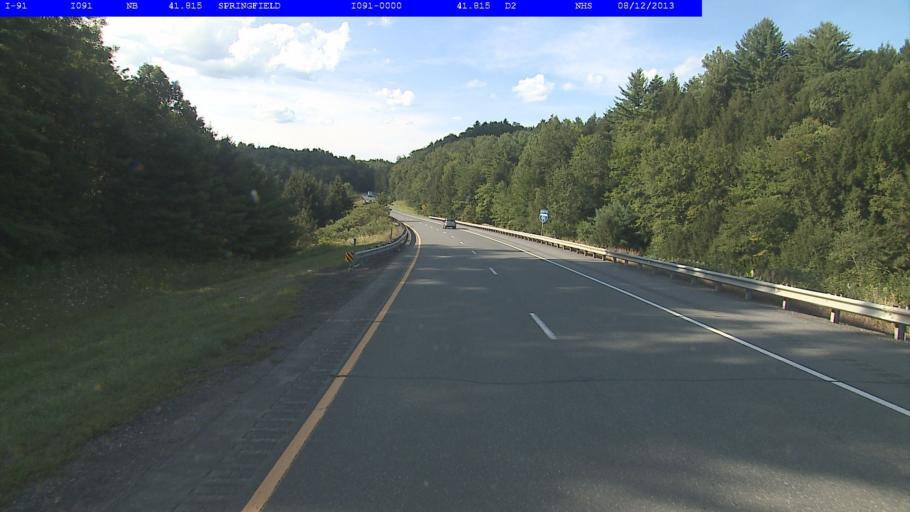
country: US
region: New Hampshire
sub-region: Sullivan County
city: Charlestown
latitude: 43.2685
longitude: -72.4326
